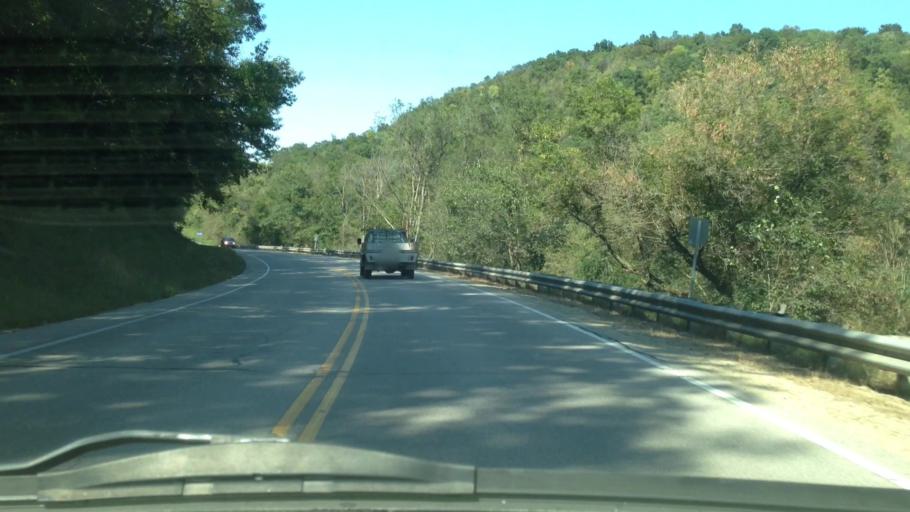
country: US
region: Minnesota
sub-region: Fillmore County
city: Rushford
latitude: 43.7657
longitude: -91.7632
